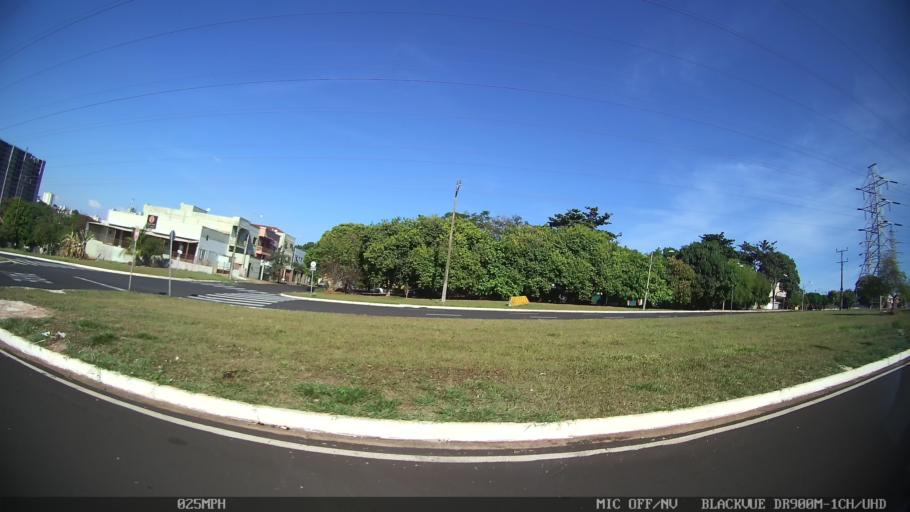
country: BR
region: Sao Paulo
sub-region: Ribeirao Preto
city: Ribeirao Preto
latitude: -21.1784
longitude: -47.7816
